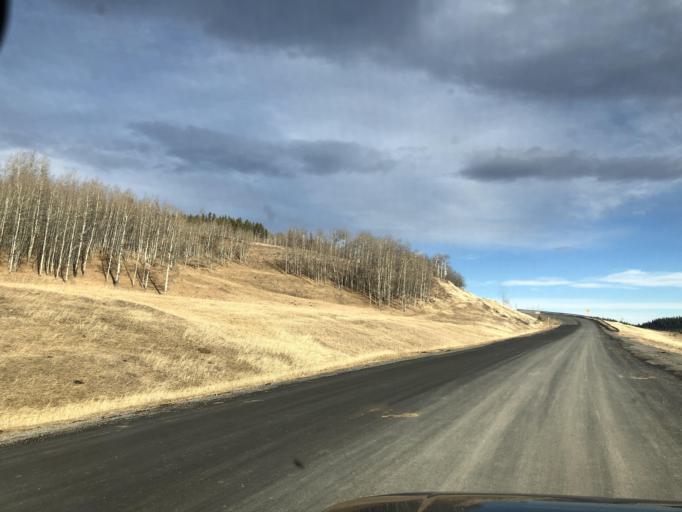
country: CA
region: Alberta
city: Cochrane
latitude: 51.0385
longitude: -114.8732
